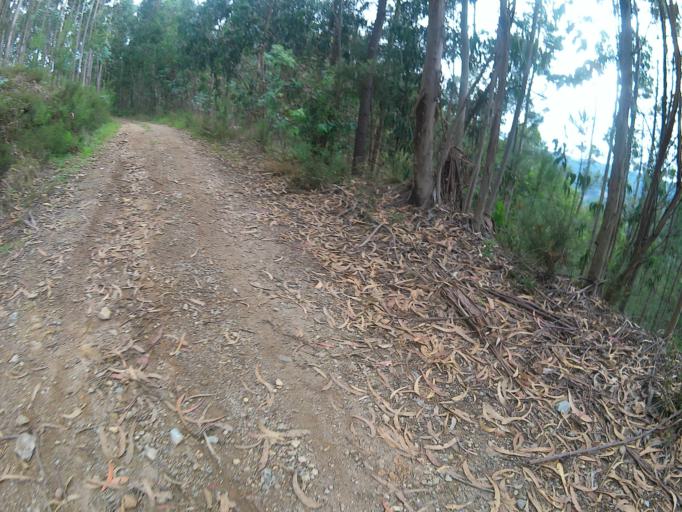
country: PT
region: Aveiro
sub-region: Albergaria-A-Velha
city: Branca
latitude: 40.7604
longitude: -8.4304
